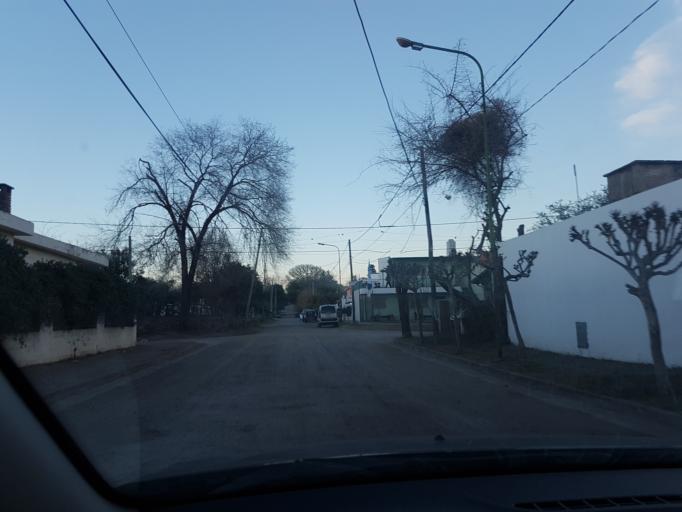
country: AR
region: Cordoba
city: Villa Allende
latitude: -31.2915
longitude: -64.3007
